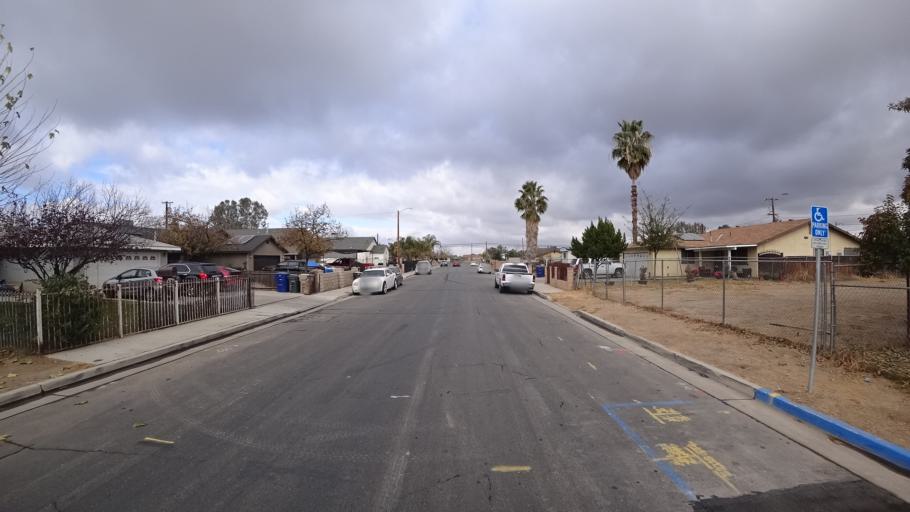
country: US
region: California
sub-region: Kern County
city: Greenfield
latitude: 35.3234
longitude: -118.9910
